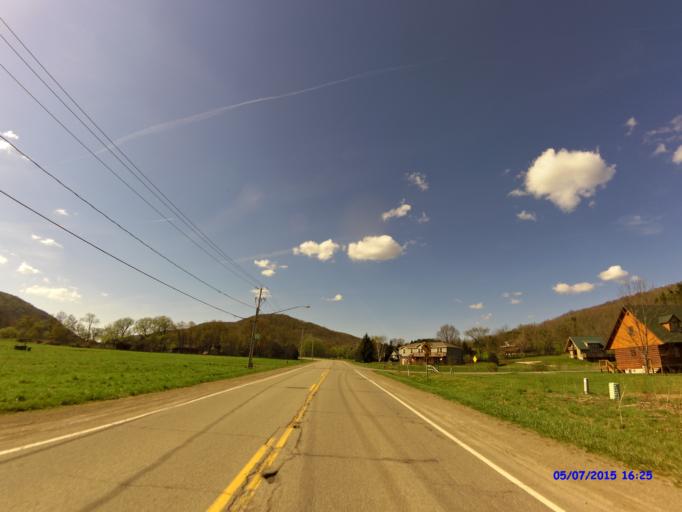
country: US
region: New York
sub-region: Cattaraugus County
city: Little Valley
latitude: 42.2866
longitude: -78.6766
